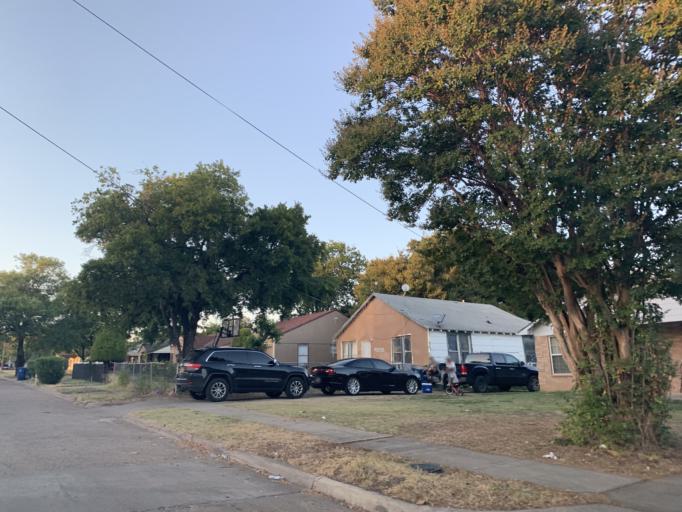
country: US
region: Texas
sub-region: Dallas County
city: Dallas
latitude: 32.6956
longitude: -96.8050
